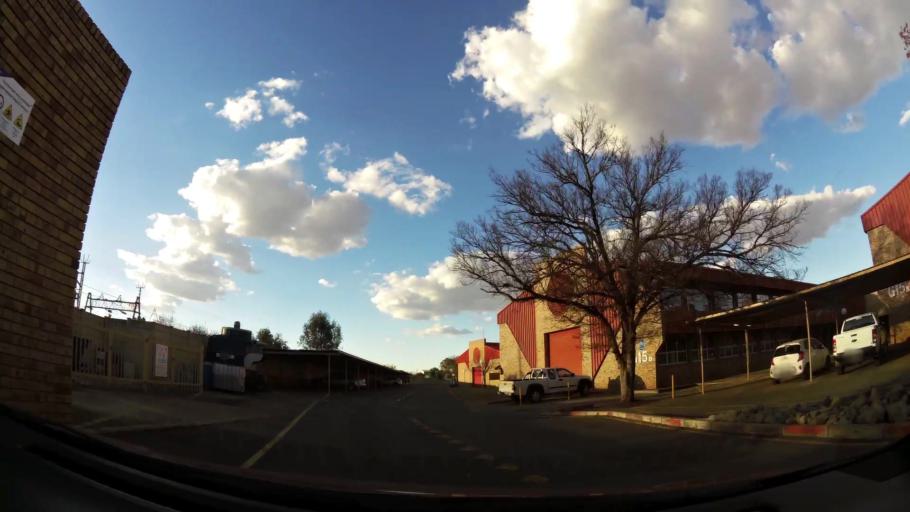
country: ZA
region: North-West
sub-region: Dr Kenneth Kaunda District Municipality
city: Potchefstroom
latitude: -26.6847
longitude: 27.0921
